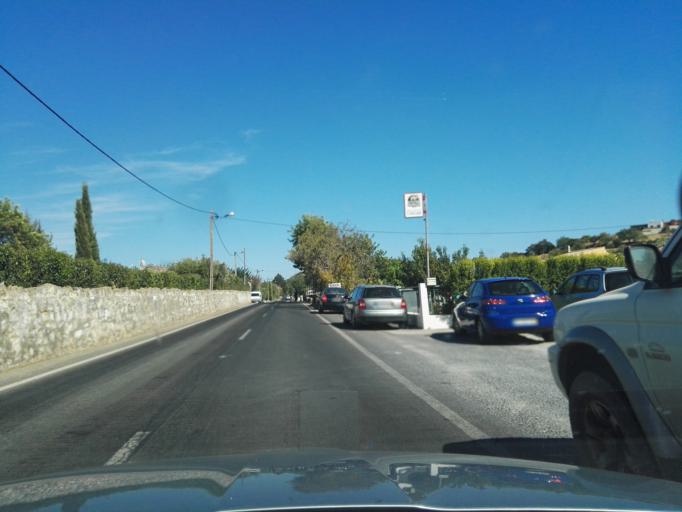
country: PT
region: Faro
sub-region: Sao Bras de Alportel
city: Sao Bras de Alportel
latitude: 37.1548
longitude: -7.8533
